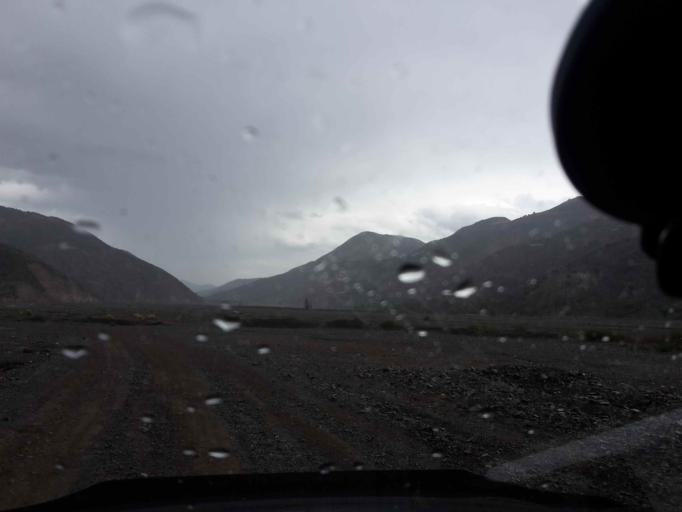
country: BO
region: Cochabamba
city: Colchani
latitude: -17.5177
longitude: -66.6205
